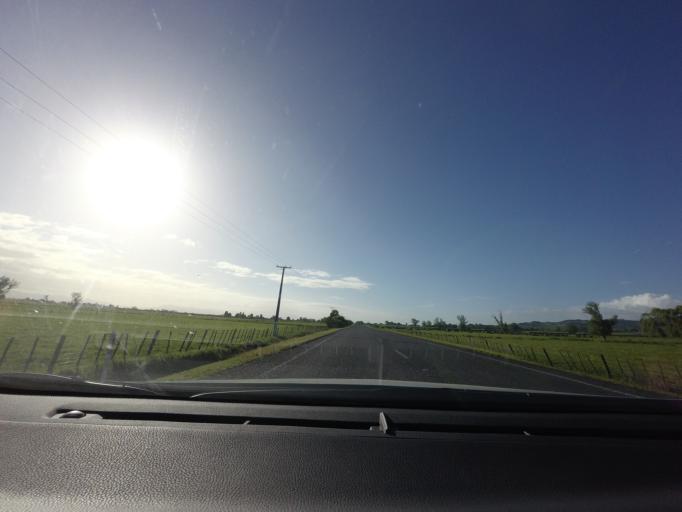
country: NZ
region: Waikato
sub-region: Hauraki District
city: Ngatea
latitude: -37.3884
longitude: 175.4542
